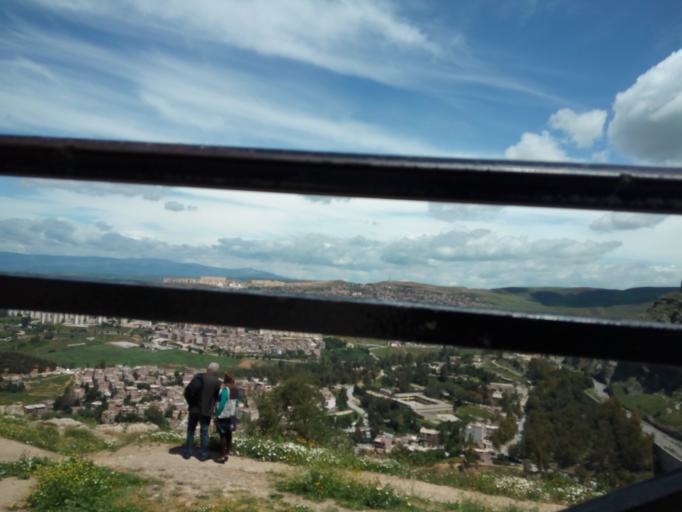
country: DZ
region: Constantine
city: Constantine
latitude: 36.3752
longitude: 6.6138
